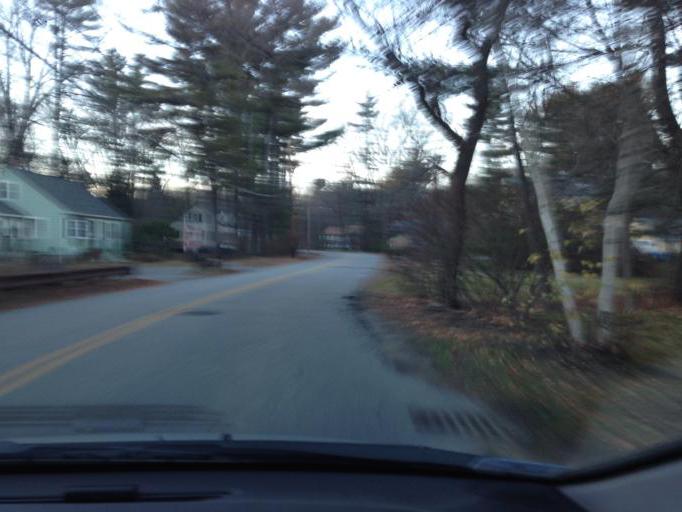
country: US
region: Massachusetts
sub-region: Middlesex County
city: Bedford
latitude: 42.4959
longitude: -71.2703
